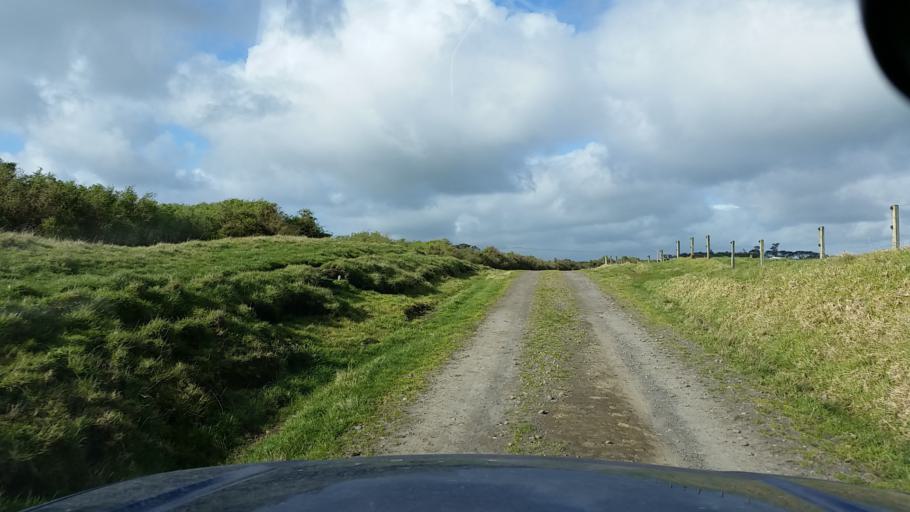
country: NZ
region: Taranaki
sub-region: South Taranaki District
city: Hawera
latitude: -39.6585
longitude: 174.3570
